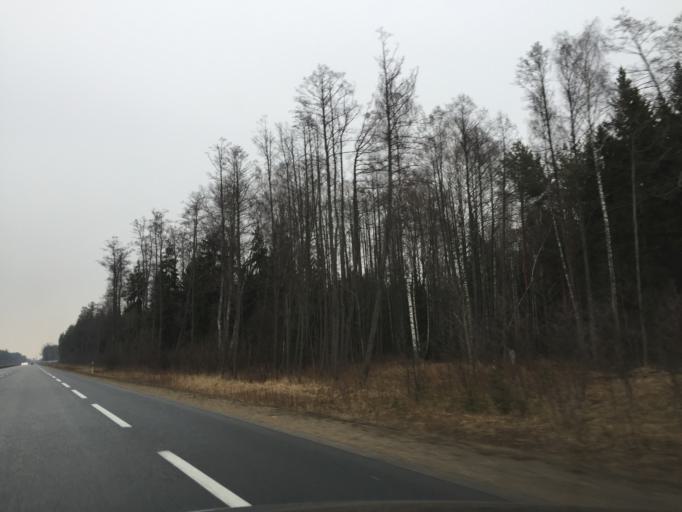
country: LV
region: Saulkrastu
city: Saulkrasti
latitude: 57.2991
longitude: 24.4396
